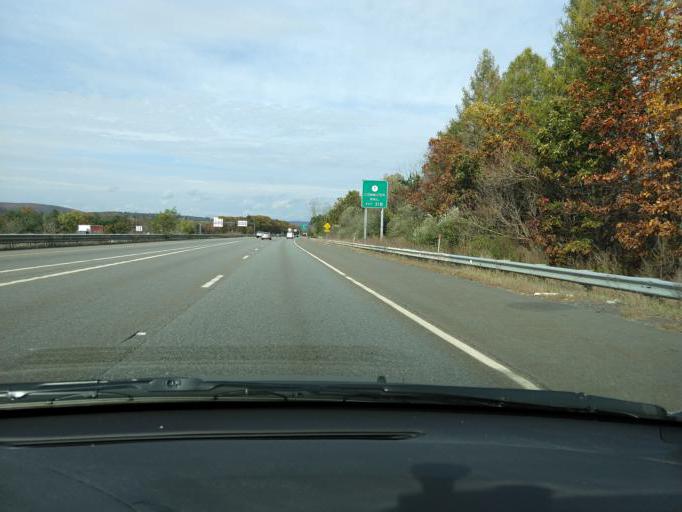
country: US
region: Massachusetts
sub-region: Worcester County
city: Leominster
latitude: 42.5277
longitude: -71.7319
